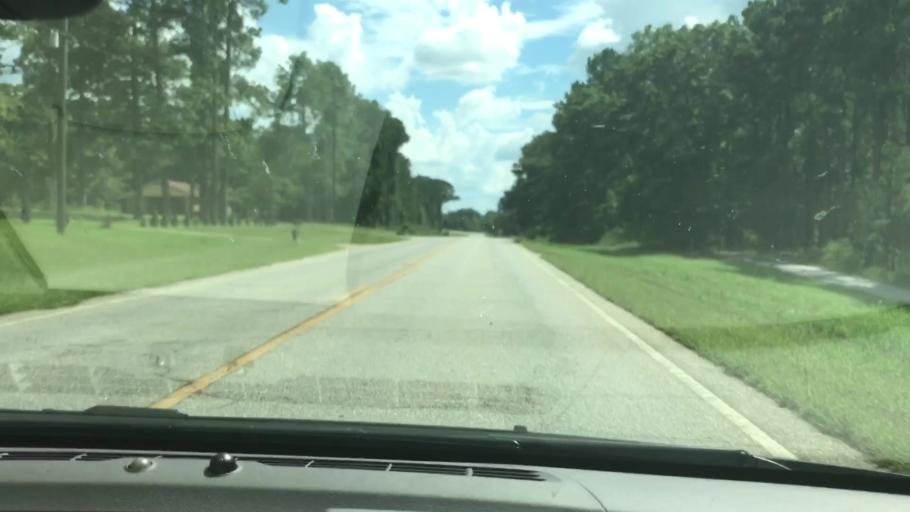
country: US
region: Georgia
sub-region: Clay County
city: Fort Gaines
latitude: 31.6581
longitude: -85.0474
